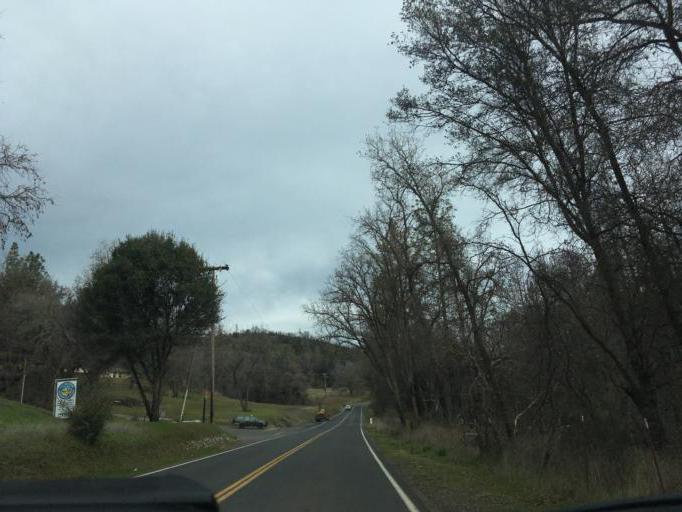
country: US
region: California
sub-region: Calaveras County
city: Mountain Ranch
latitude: 38.2017
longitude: -120.5809
